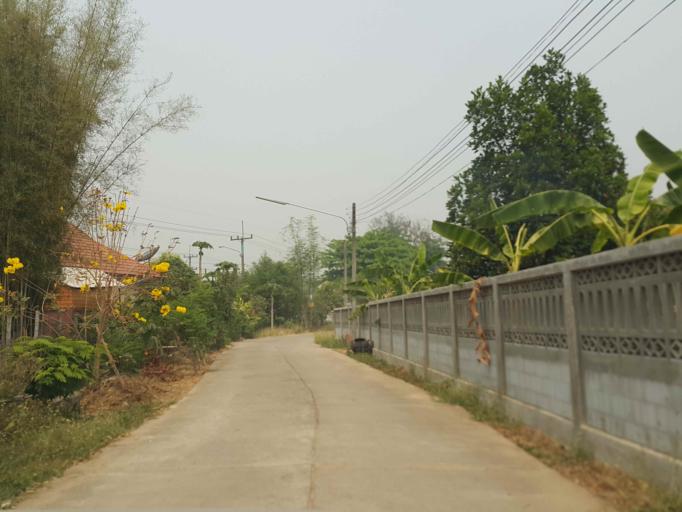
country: TH
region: Chiang Mai
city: Mae Taeng
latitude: 19.0778
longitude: 98.9383
